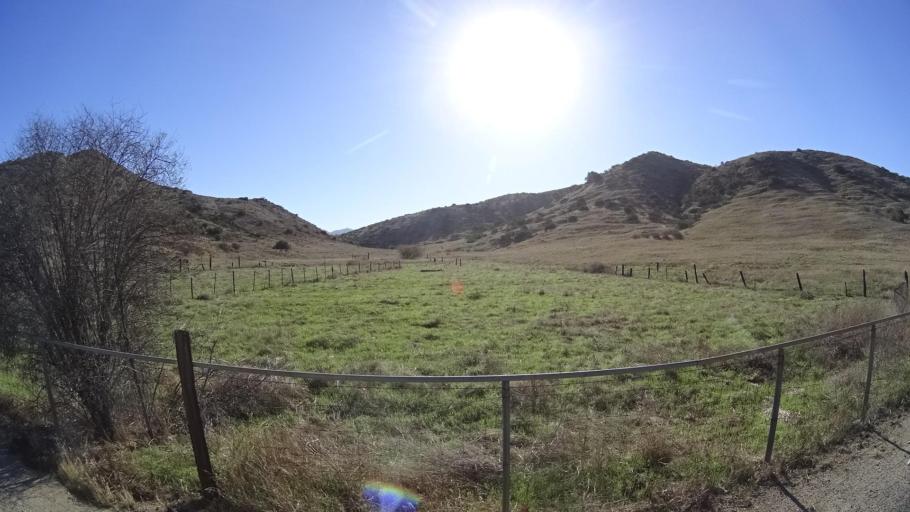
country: US
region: California
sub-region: San Diego County
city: Jamul
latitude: 32.6620
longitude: -116.8380
